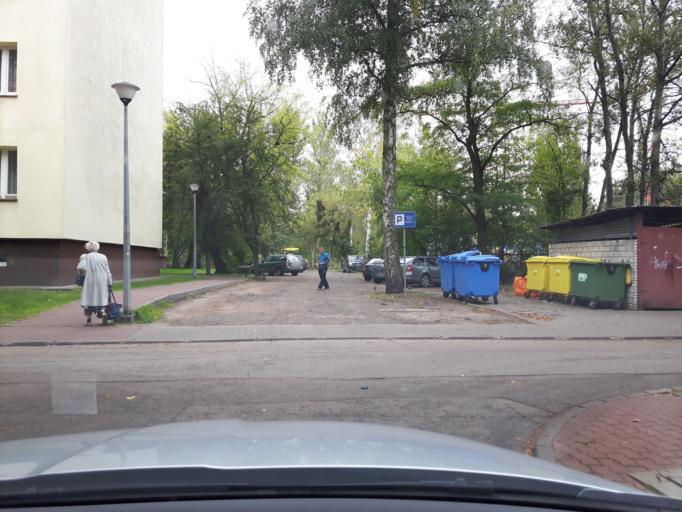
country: PL
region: Masovian Voivodeship
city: Zielonka
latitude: 52.3015
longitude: 21.1621
